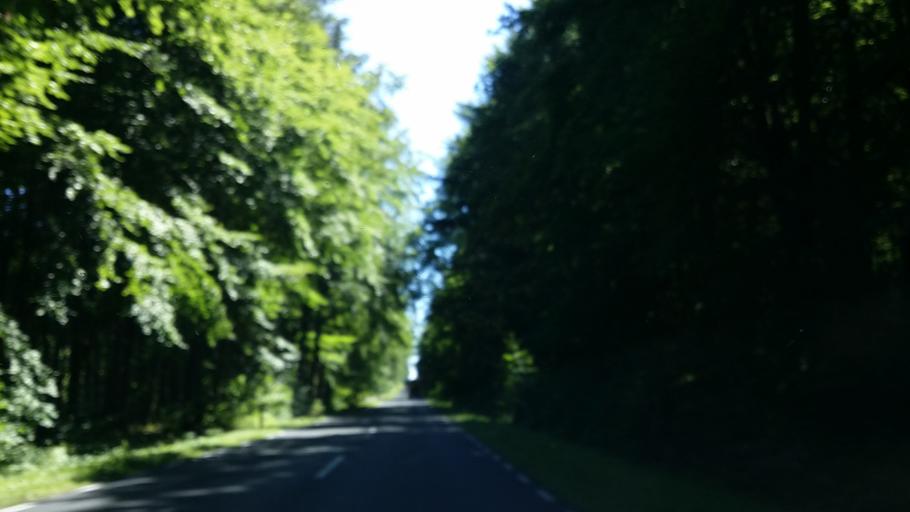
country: PL
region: West Pomeranian Voivodeship
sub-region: Powiat kolobrzeski
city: Goscino
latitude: 54.1056
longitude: 15.6062
